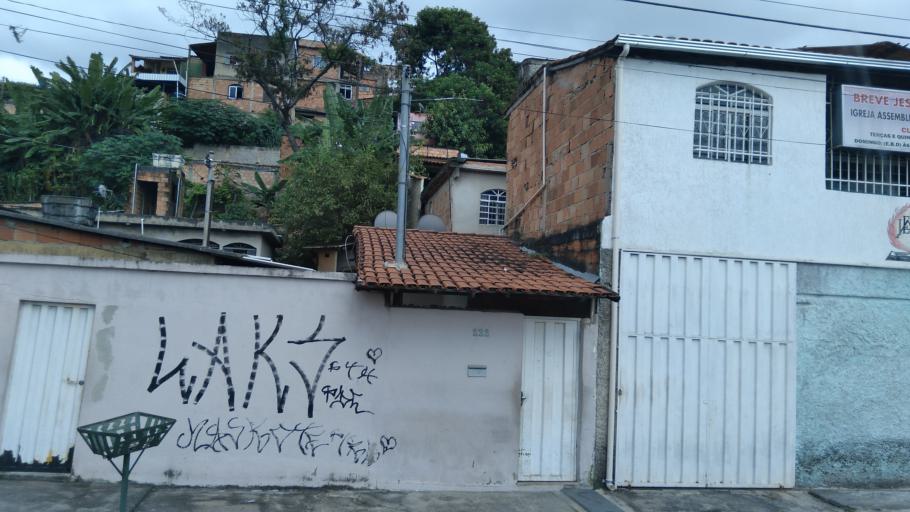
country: BR
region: Minas Gerais
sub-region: Belo Horizonte
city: Belo Horizonte
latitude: -19.8638
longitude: -43.9127
